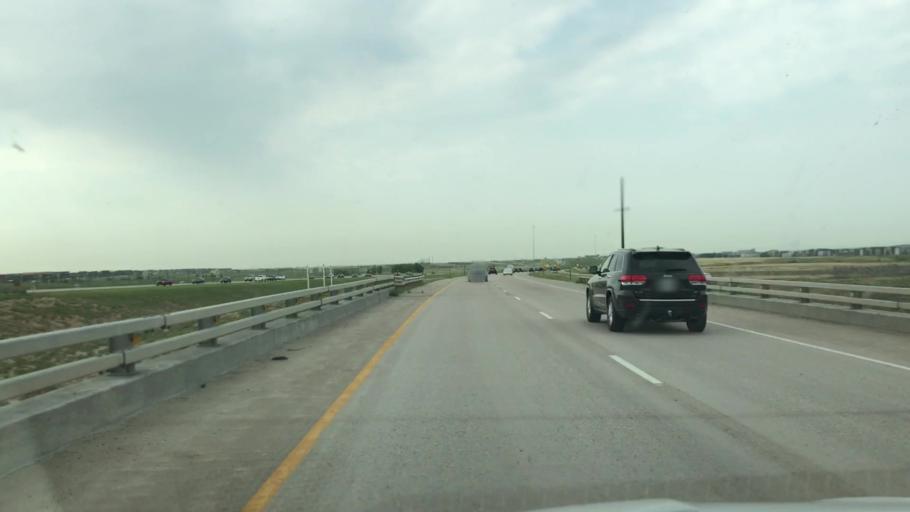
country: US
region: Colorado
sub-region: Adams County
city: Aurora
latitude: 39.7982
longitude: -104.7871
